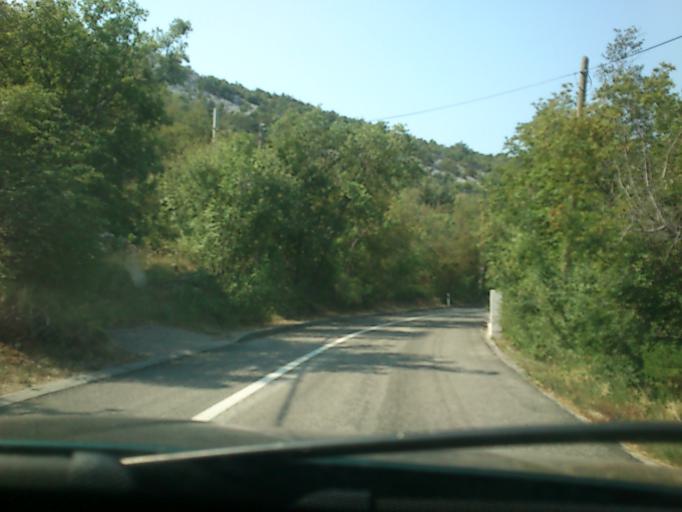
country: HR
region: Primorsko-Goranska
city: Banjol
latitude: 44.7046
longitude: 14.9018
